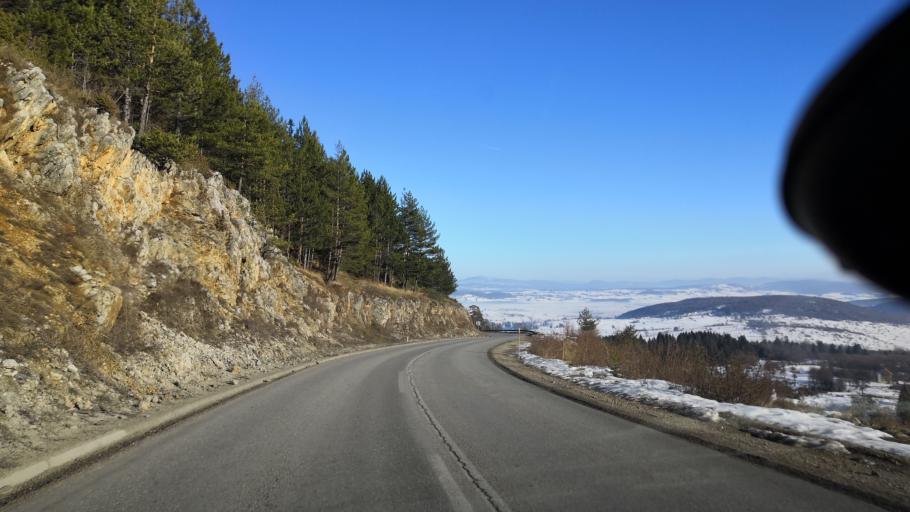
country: BA
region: Republika Srpska
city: Sokolac
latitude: 43.9182
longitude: 18.7358
